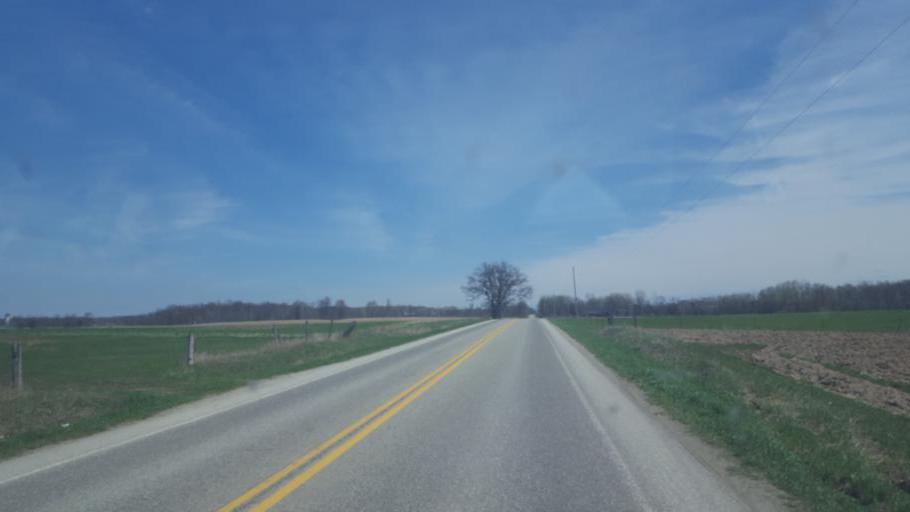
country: US
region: Michigan
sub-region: Midland County
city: Coleman
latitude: 43.8730
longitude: -84.6437
